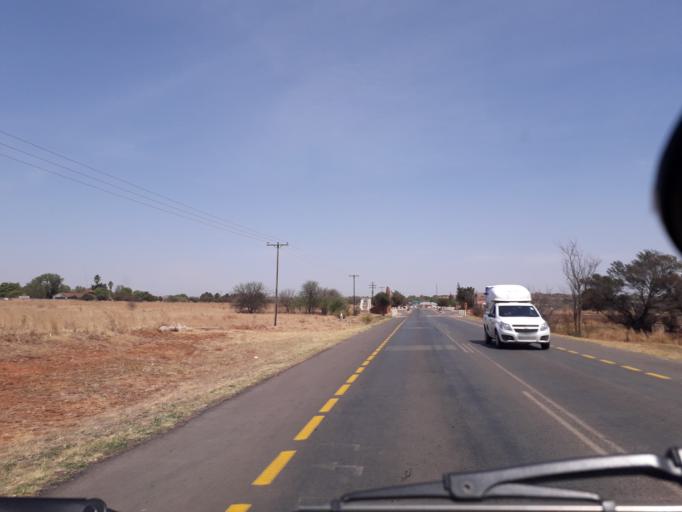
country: ZA
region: Gauteng
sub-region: West Rand District Municipality
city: Krugersdorp
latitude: -26.0206
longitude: 27.7258
